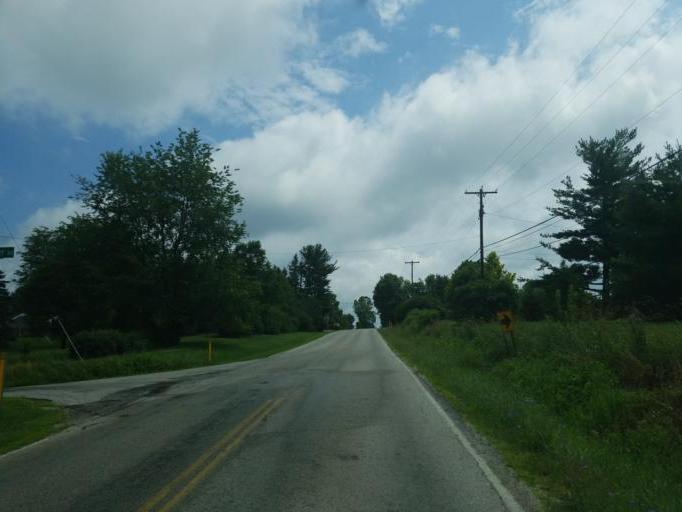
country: US
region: Ohio
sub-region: Richland County
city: Ontario
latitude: 40.7223
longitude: -82.6006
